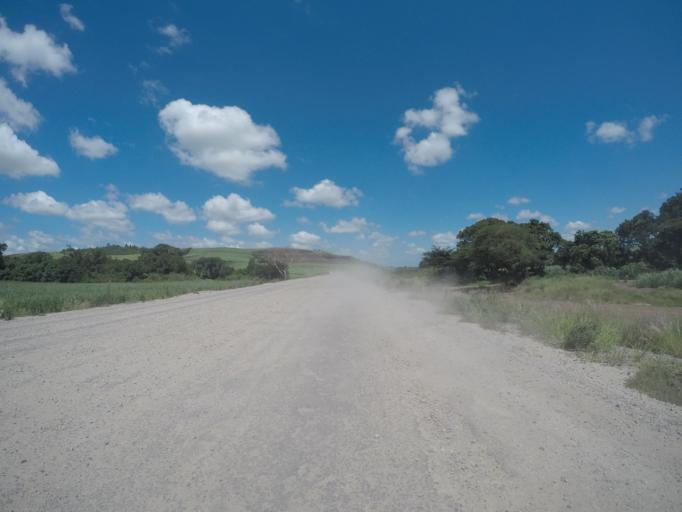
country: ZA
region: KwaZulu-Natal
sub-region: uThungulu District Municipality
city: Empangeni
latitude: -28.6456
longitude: 31.7668
